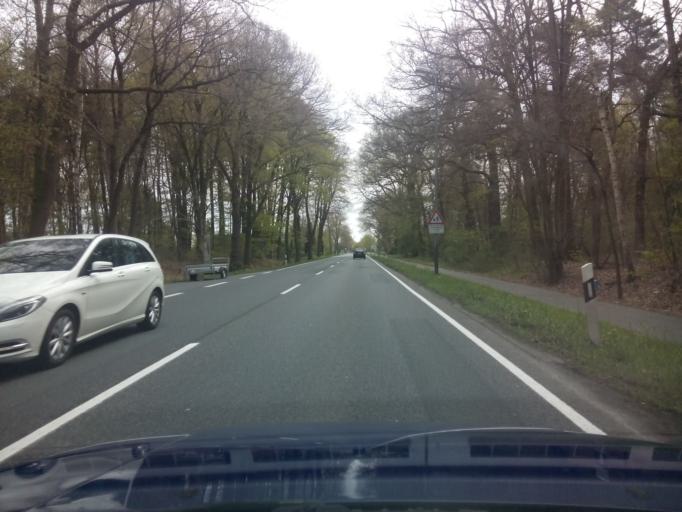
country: DE
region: Lower Saxony
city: Syke
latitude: 52.9603
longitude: 8.8019
